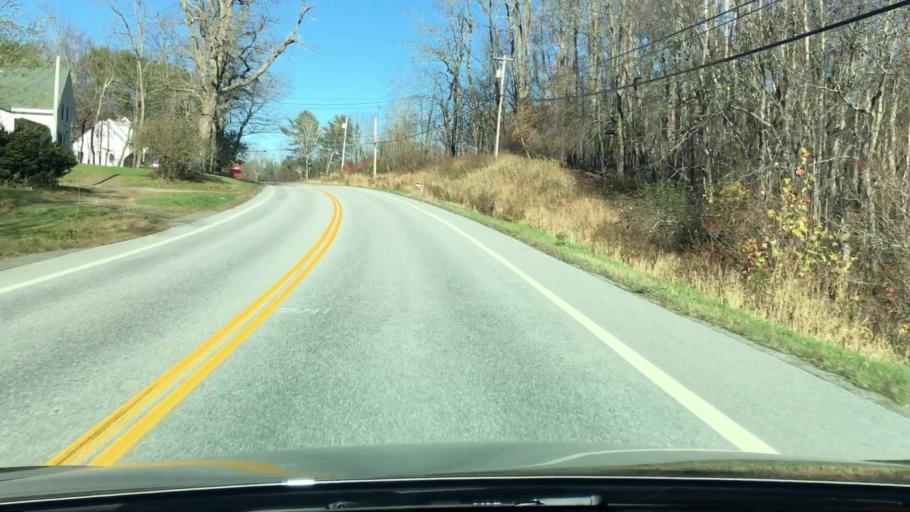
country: US
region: Maine
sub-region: Waldo County
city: Winterport
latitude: 44.6405
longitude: -68.8271
